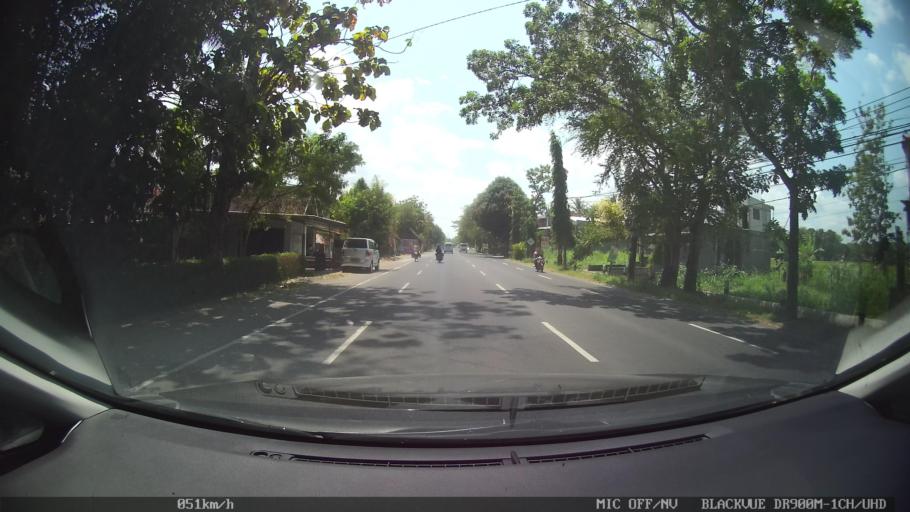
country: ID
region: Daerah Istimewa Yogyakarta
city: Bambanglipuro
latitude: -7.9282
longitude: 110.2759
